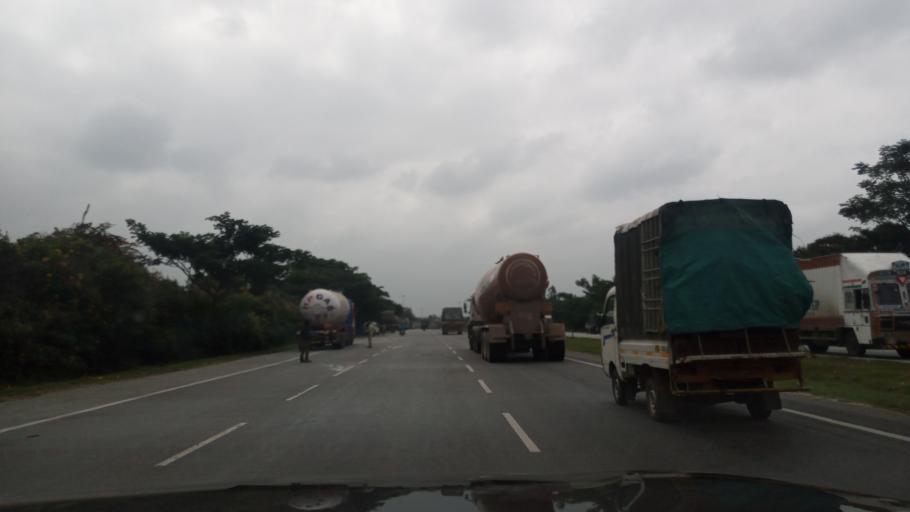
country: IN
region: Karnataka
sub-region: Bangalore Rural
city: Nelamangala
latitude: 13.0504
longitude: 77.4763
